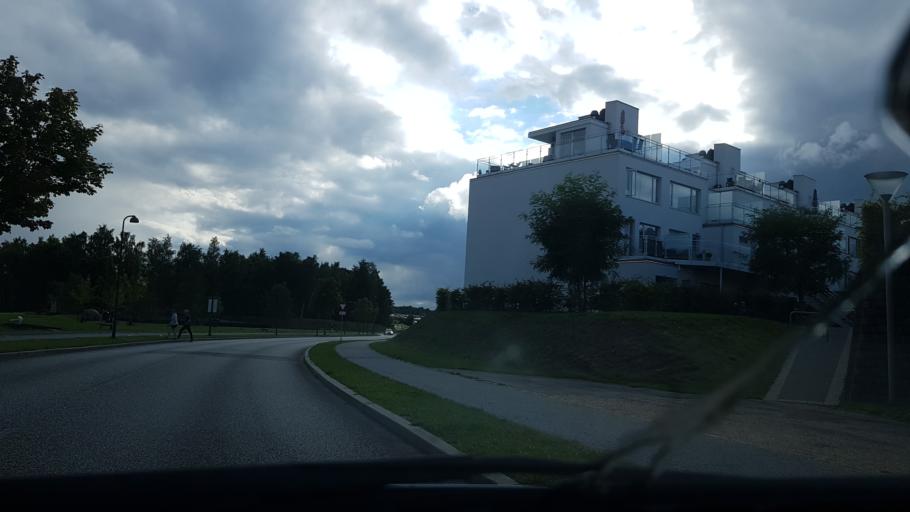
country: DK
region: Capital Region
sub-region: Fredensborg Kommune
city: Kokkedal
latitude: 55.9070
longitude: 12.4895
